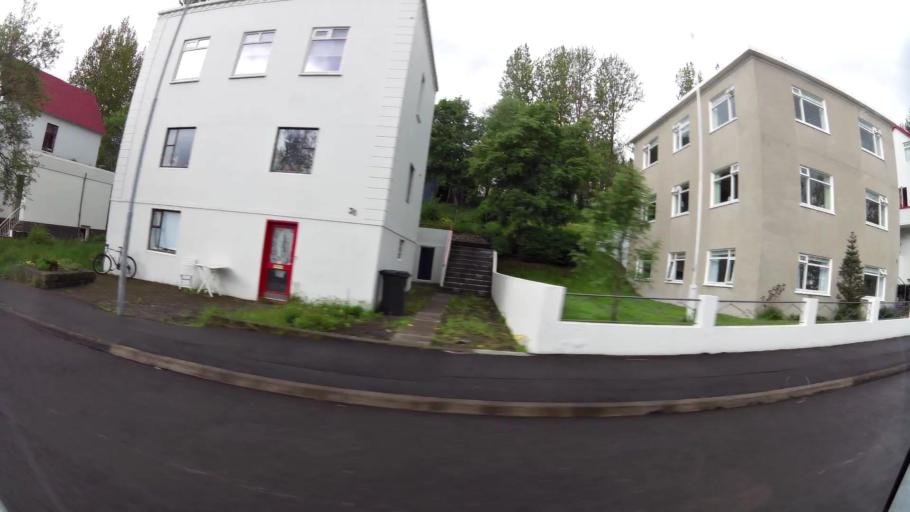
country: IS
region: Northeast
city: Akureyri
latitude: 65.6850
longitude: -18.0966
